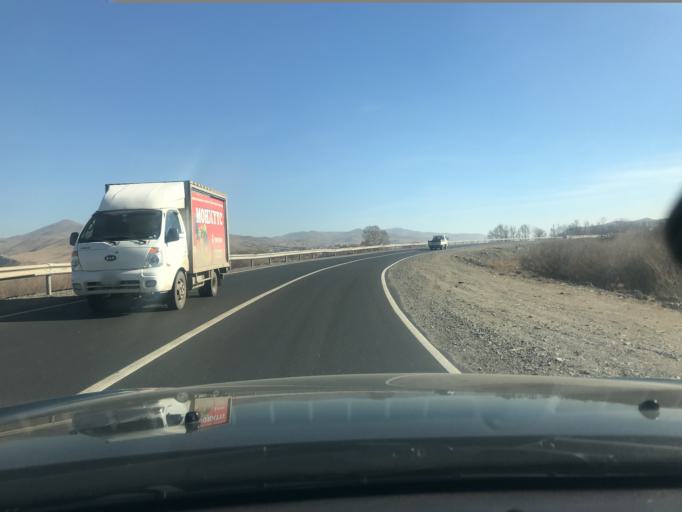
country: MN
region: Ulaanbaatar
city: Ulaanbaatar
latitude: 47.8961
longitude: 107.0628
